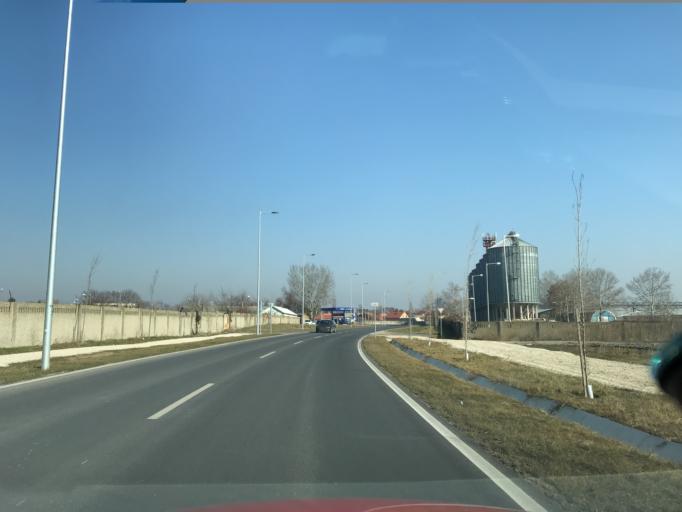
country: HU
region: Gyor-Moson-Sopron
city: Gyor
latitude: 47.6781
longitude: 17.6084
